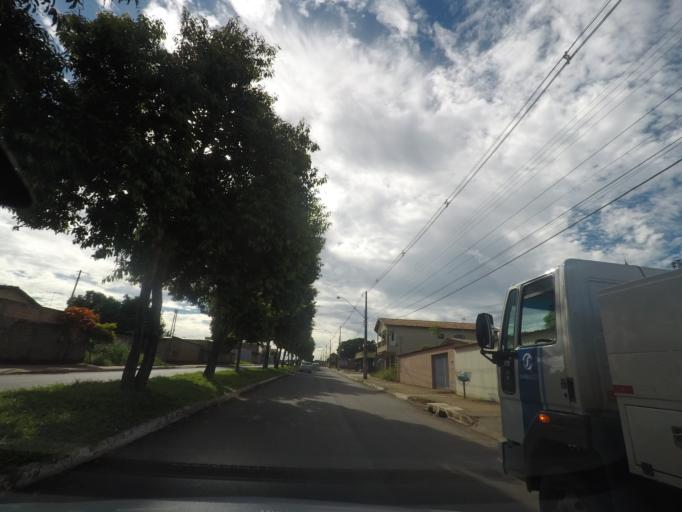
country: BR
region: Goias
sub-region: Aparecida De Goiania
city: Aparecida de Goiania
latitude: -16.8187
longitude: -49.2990
